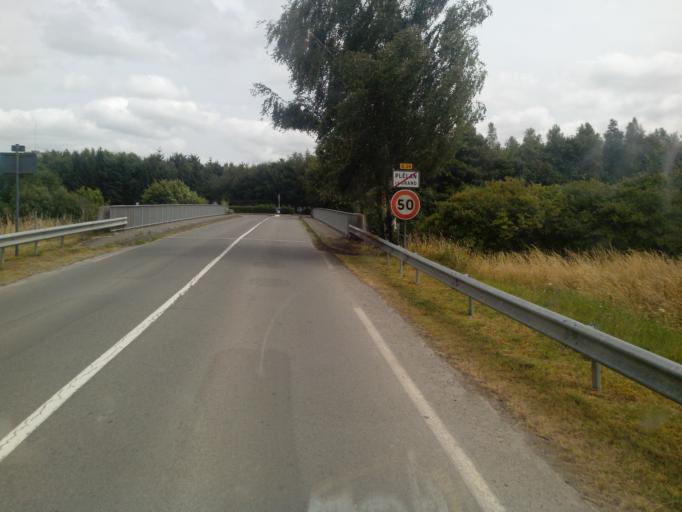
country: FR
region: Brittany
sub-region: Departement d'Ille-et-Vilaine
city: Plelan-le-Grand
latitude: 48.0001
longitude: -2.0929
